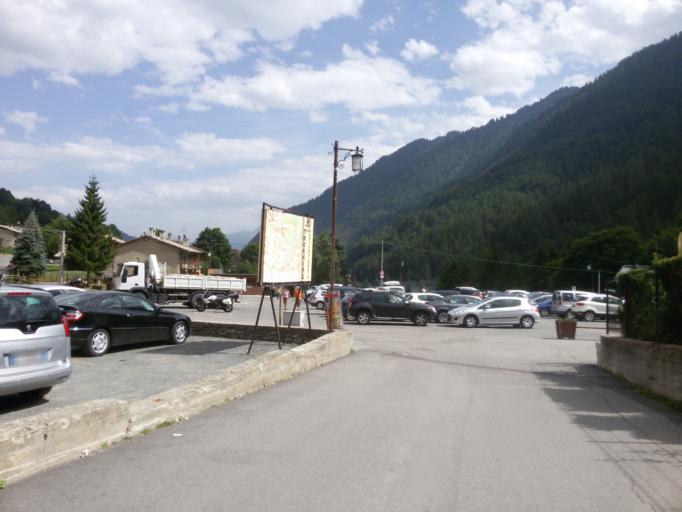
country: IT
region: Piedmont
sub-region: Provincia di Cuneo
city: Pontechianale
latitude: 44.6224
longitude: 7.0296
